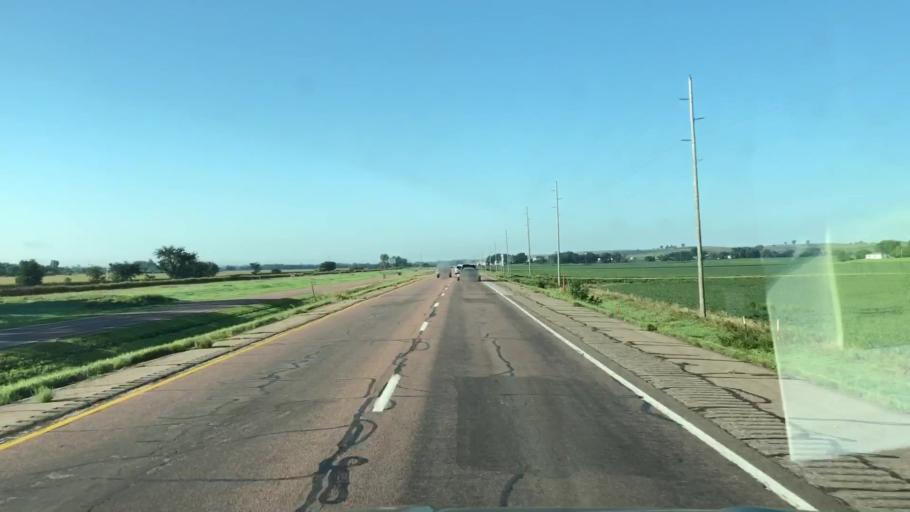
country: US
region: Iowa
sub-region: Plymouth County
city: Le Mars
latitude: 42.6795
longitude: -96.2694
